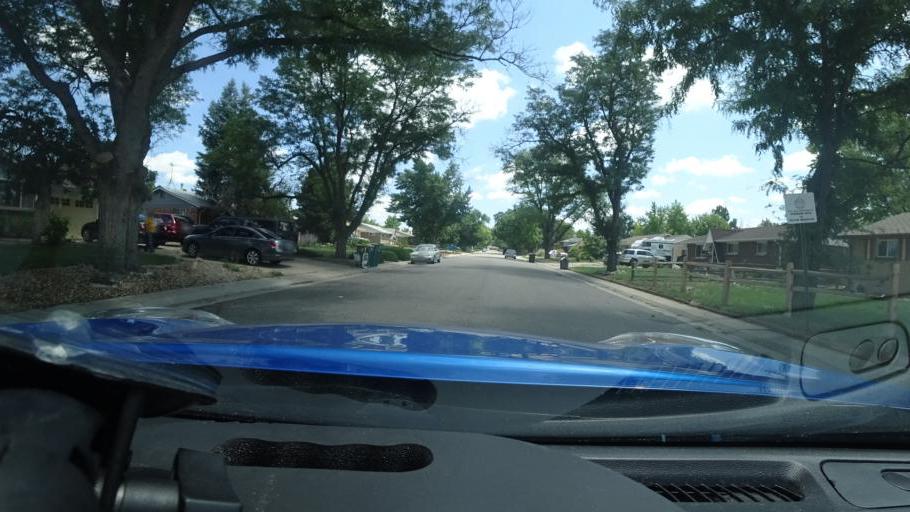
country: US
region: Colorado
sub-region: Adams County
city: Aurora
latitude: 39.7104
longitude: -104.8470
